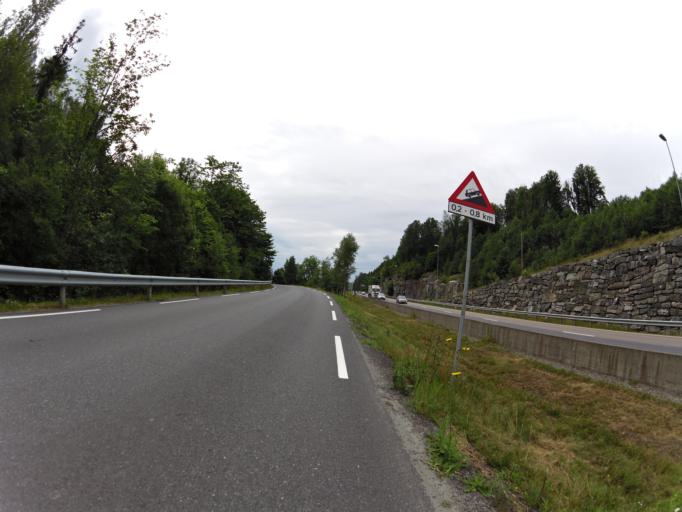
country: NO
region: Akershus
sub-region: As
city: As
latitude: 59.7031
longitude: 10.7380
